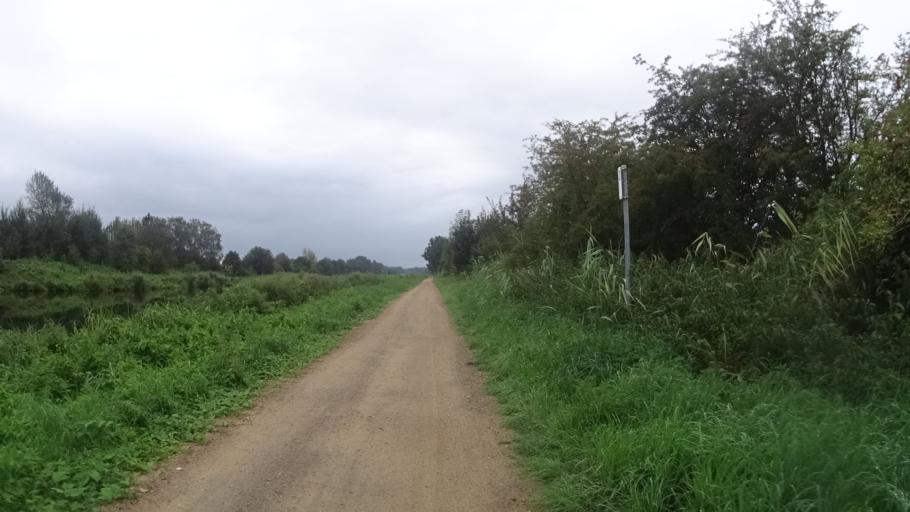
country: DE
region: Schleswig-Holstein
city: Witzeeze
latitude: 53.4453
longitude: 10.6197
